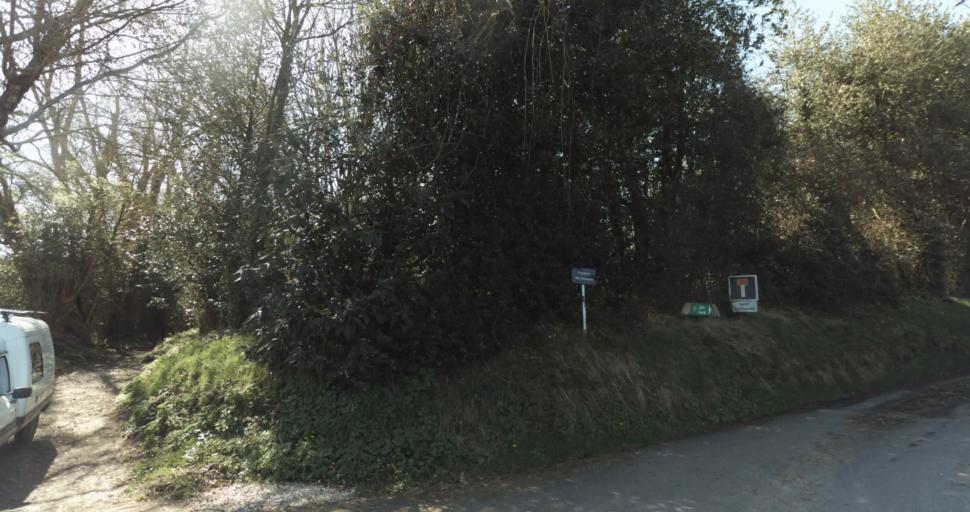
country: FR
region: Lower Normandy
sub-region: Departement du Calvados
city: Saint-Pierre-sur-Dives
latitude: 49.0122
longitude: 0.0438
